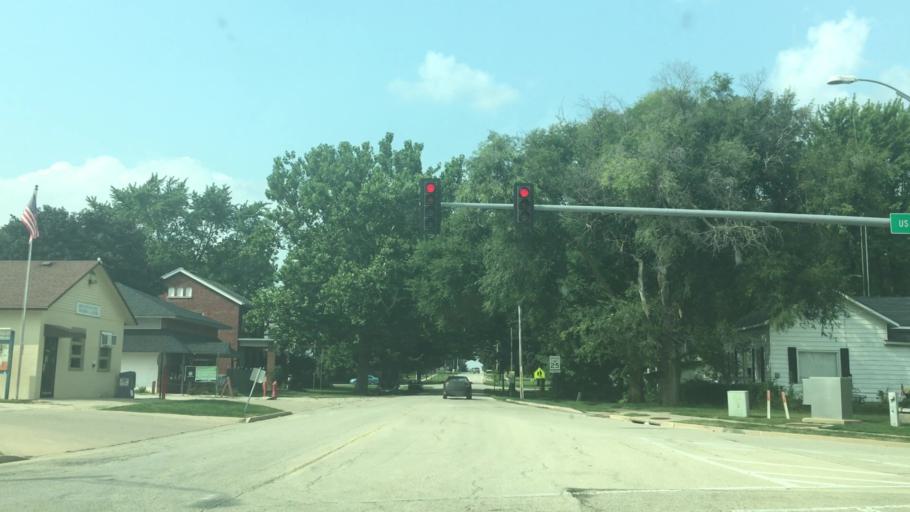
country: US
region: Illinois
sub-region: DeKalb County
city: Waterman
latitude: 41.7692
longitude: -88.7738
